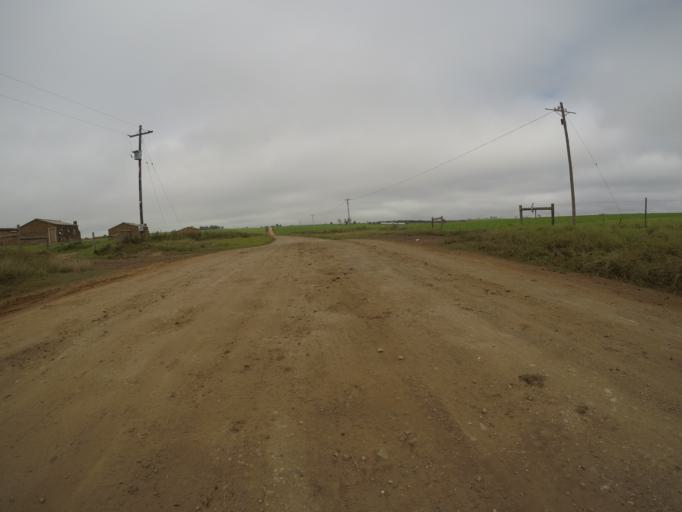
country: ZA
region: Eastern Cape
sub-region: Cacadu District Municipality
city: Kareedouw
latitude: -34.0234
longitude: 24.2407
